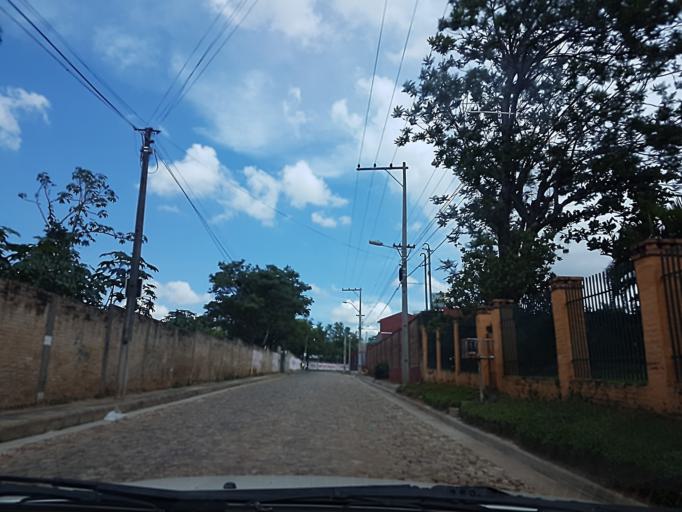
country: PY
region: Central
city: Colonia Mariano Roque Alonso
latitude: -25.2300
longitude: -57.5287
